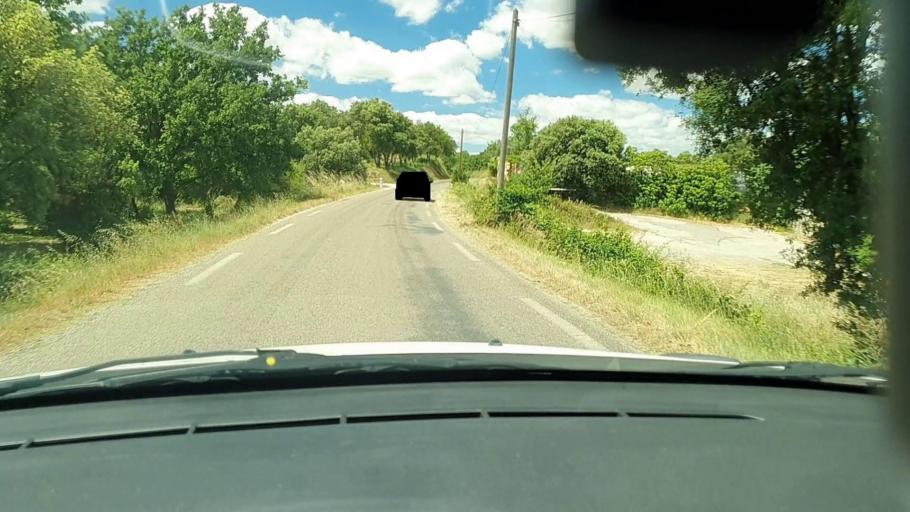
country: FR
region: Languedoc-Roussillon
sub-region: Departement du Gard
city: Cabrieres
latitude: 43.9545
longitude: 4.4542
